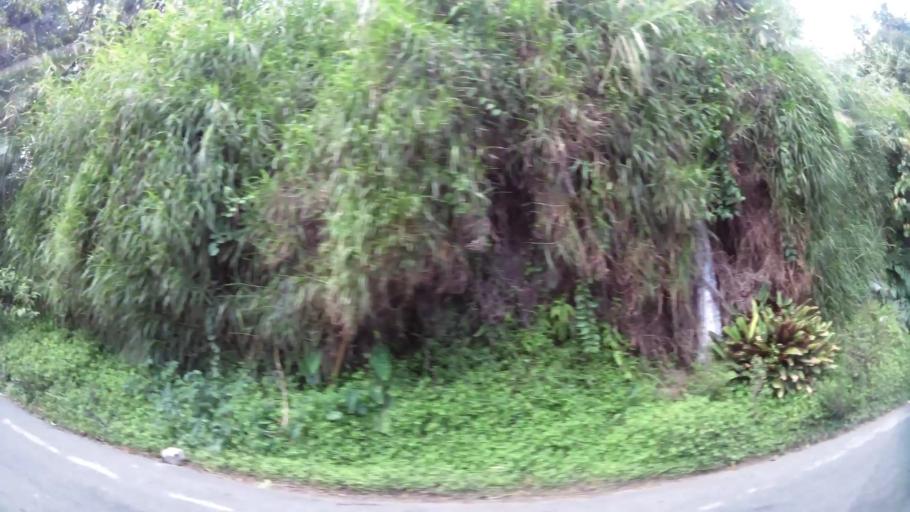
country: CO
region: Antioquia
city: La Estrella
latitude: 6.1568
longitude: -75.6339
